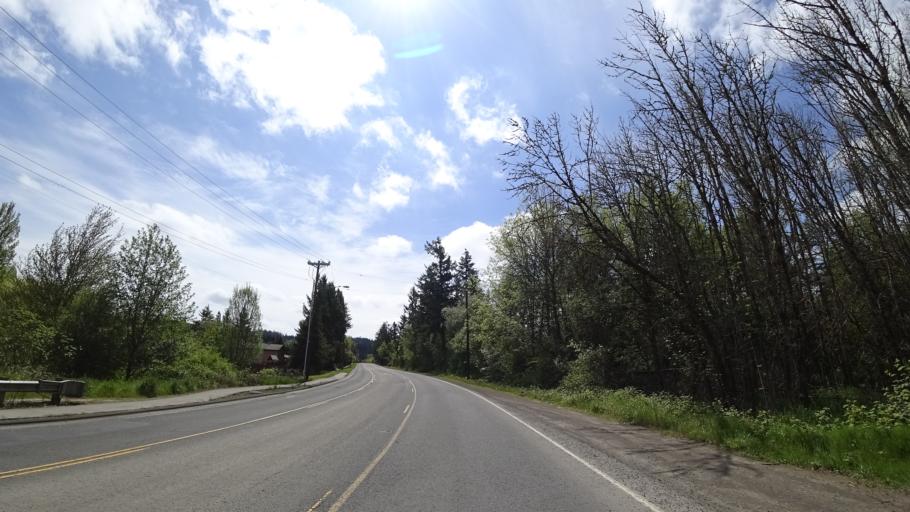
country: US
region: Oregon
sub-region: Washington County
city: Aloha
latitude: 45.4730
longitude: -122.8952
